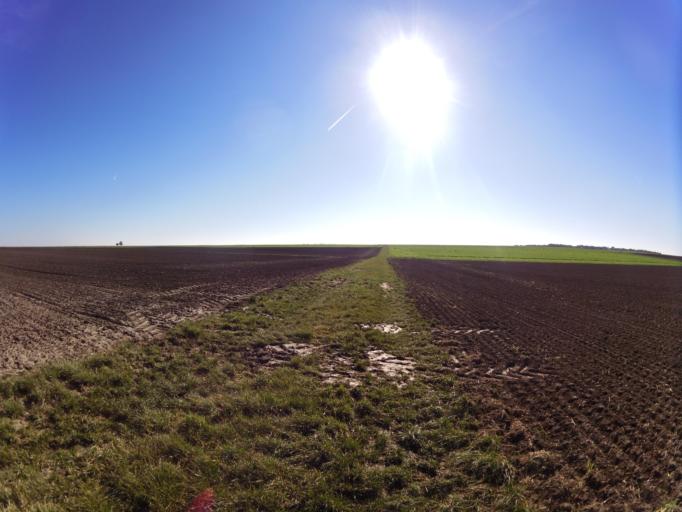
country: DE
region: Bavaria
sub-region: Regierungsbezirk Unterfranken
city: Geroldshausen
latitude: 49.6852
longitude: 9.9147
